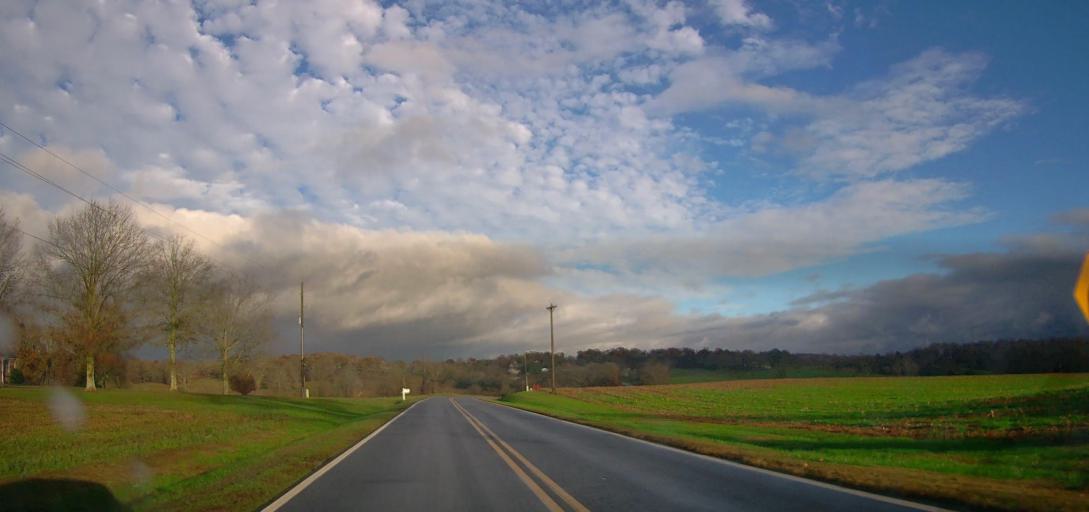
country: US
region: Georgia
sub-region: White County
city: Cleveland
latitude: 34.5465
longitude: -83.7075
